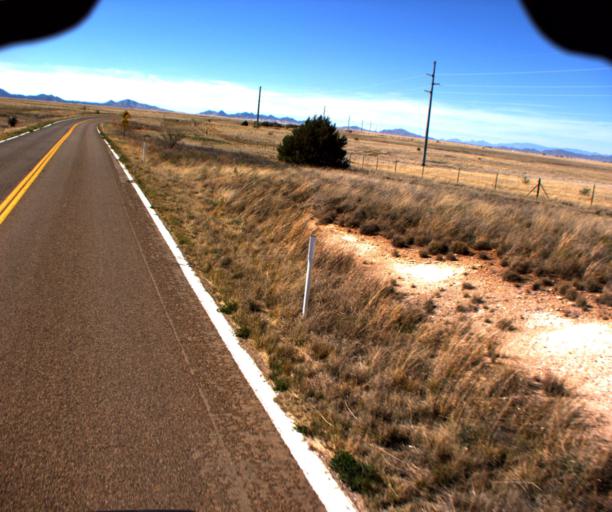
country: US
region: Arizona
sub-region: Cochise County
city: Huachuca City
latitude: 31.6214
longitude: -110.5893
